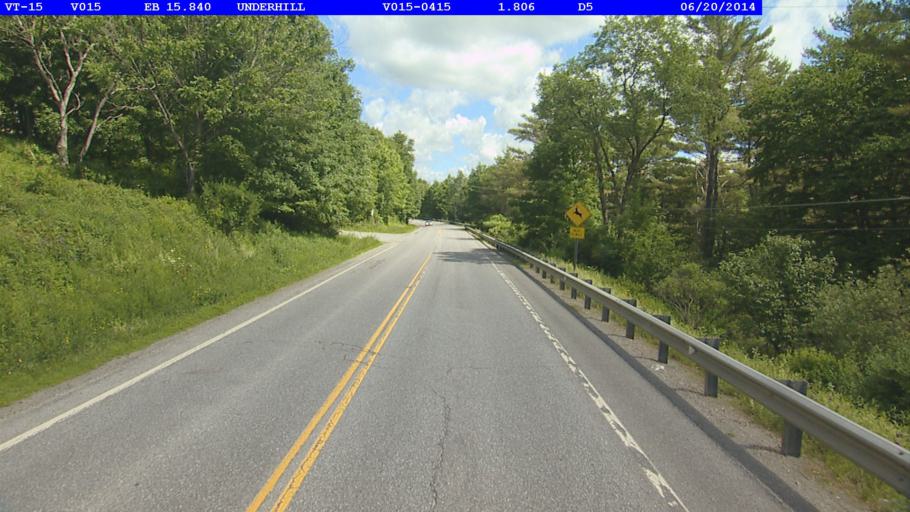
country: US
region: Vermont
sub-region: Chittenden County
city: Jericho
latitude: 44.5500
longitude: -72.9454
